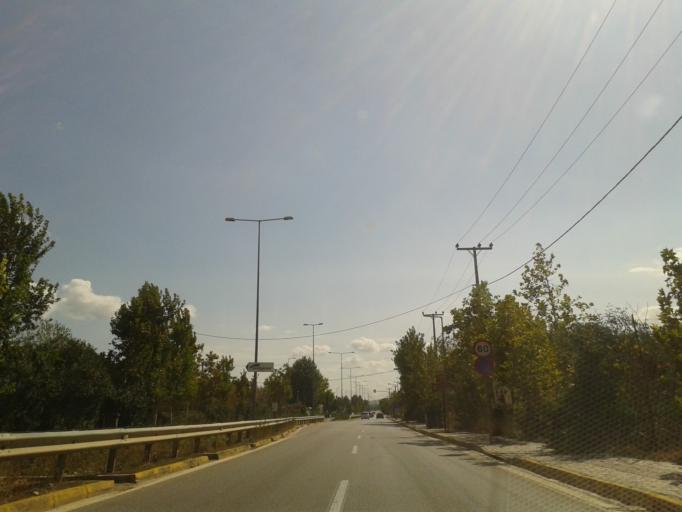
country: GR
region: Attica
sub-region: Nomarchia Anatolikis Attikis
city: Vrana
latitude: 38.1339
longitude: 23.9677
